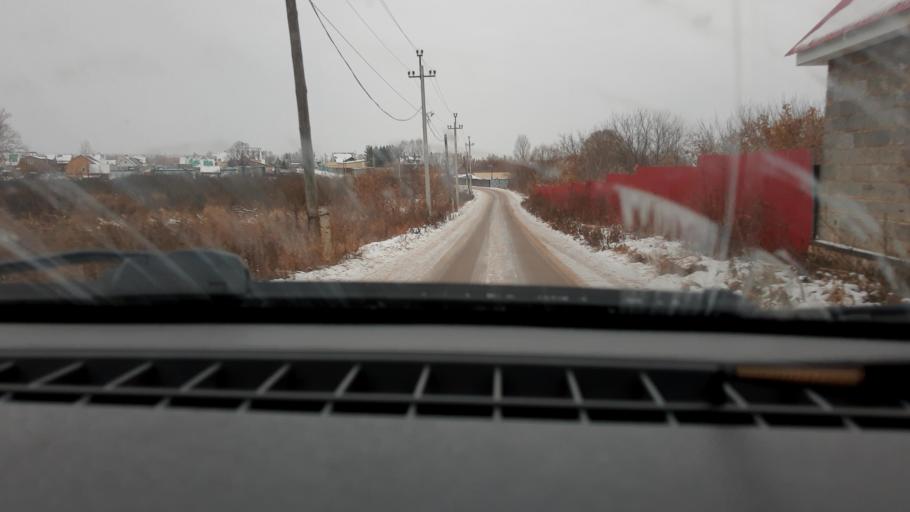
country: RU
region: Bashkortostan
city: Kabakovo
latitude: 54.7017
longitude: 56.2522
